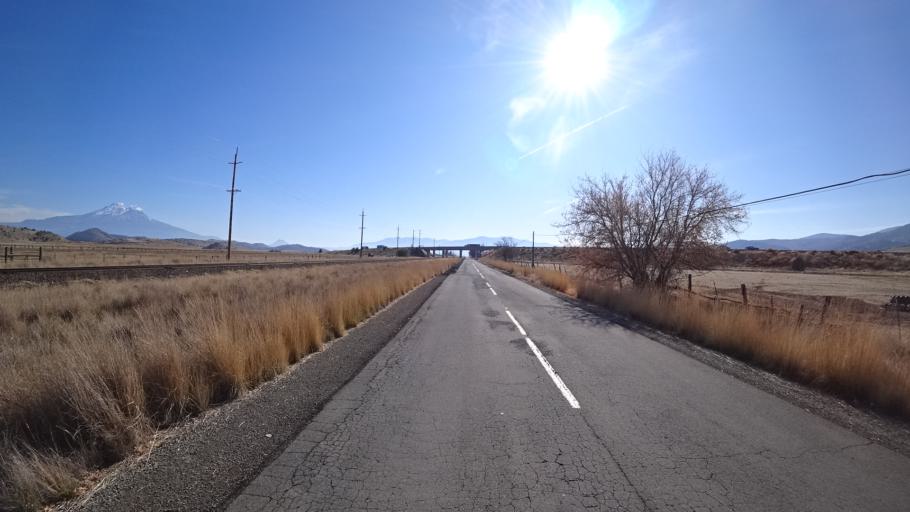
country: US
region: California
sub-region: Siskiyou County
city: Montague
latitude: 41.6305
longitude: -122.5220
